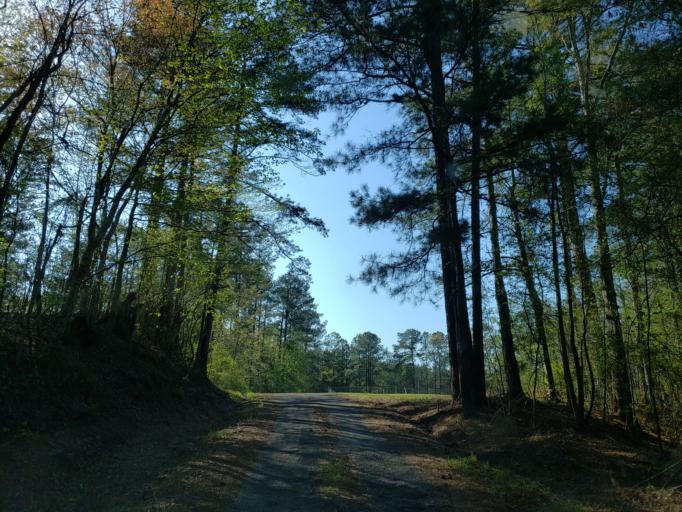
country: US
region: Mississippi
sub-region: Smith County
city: Taylorsville
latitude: 31.6891
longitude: -89.4169
